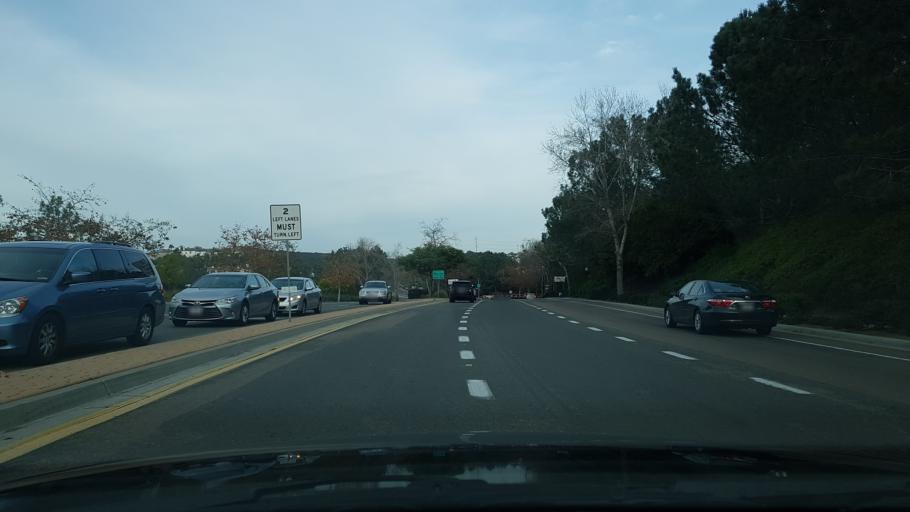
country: US
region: California
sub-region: San Diego County
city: Del Mar
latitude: 32.9208
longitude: -117.2306
